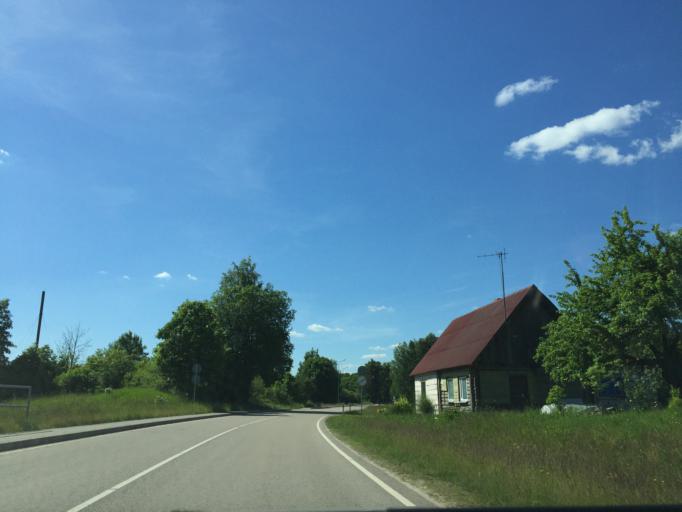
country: LV
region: Preilu Rajons
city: Jaunaglona
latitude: 56.2396
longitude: 27.2191
